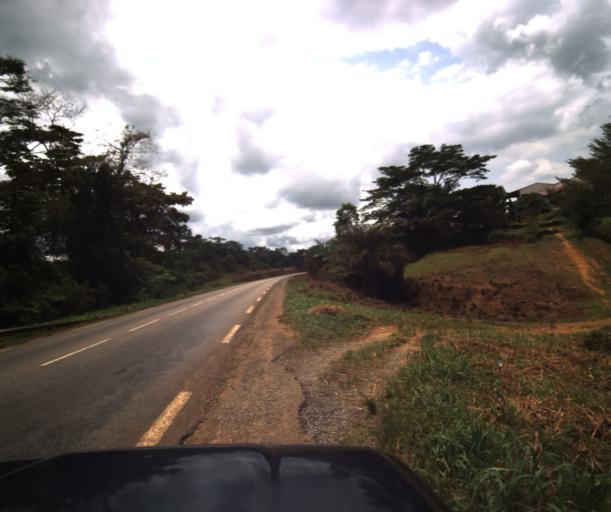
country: CM
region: Centre
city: Eseka
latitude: 3.8488
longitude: 10.4985
